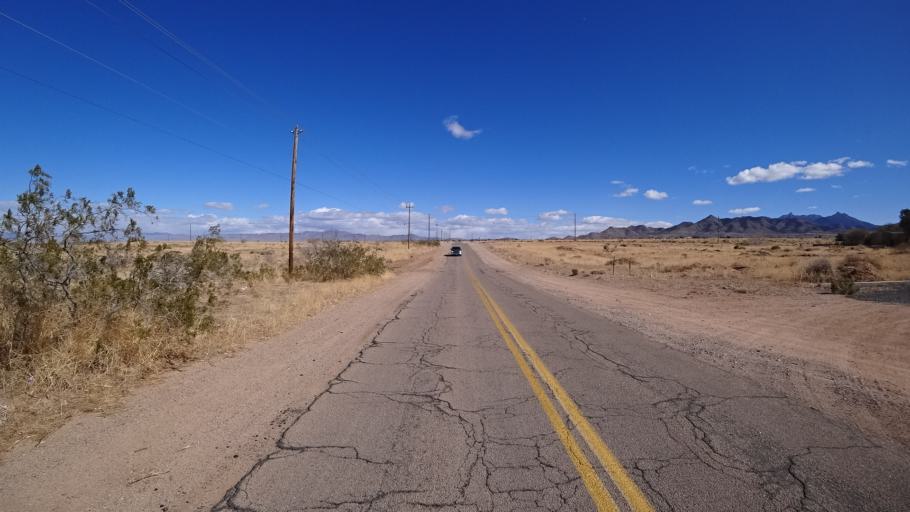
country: US
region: Arizona
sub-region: Mohave County
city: Kingman
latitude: 35.1990
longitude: -113.9954
